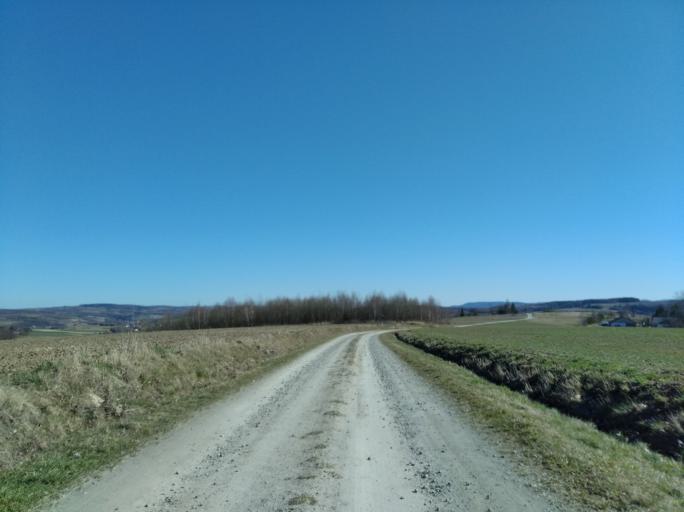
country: PL
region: Subcarpathian Voivodeship
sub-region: Powiat strzyzowski
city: Wisniowa
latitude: 49.9218
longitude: 21.6744
